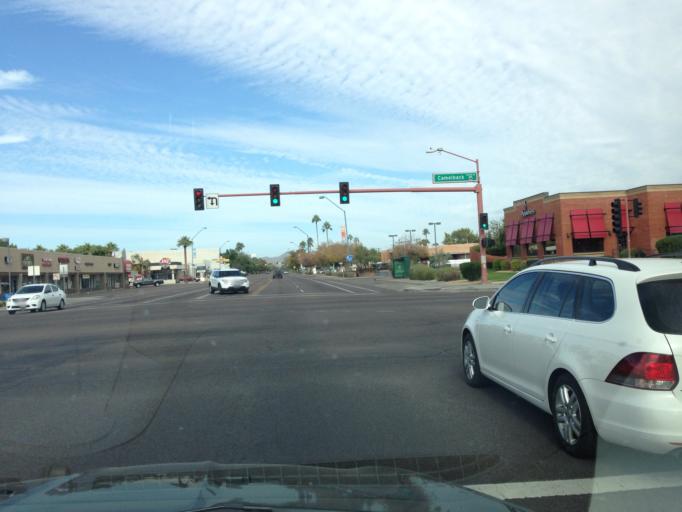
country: US
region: Arizona
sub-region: Maricopa County
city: Phoenix
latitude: 33.5091
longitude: -112.0737
